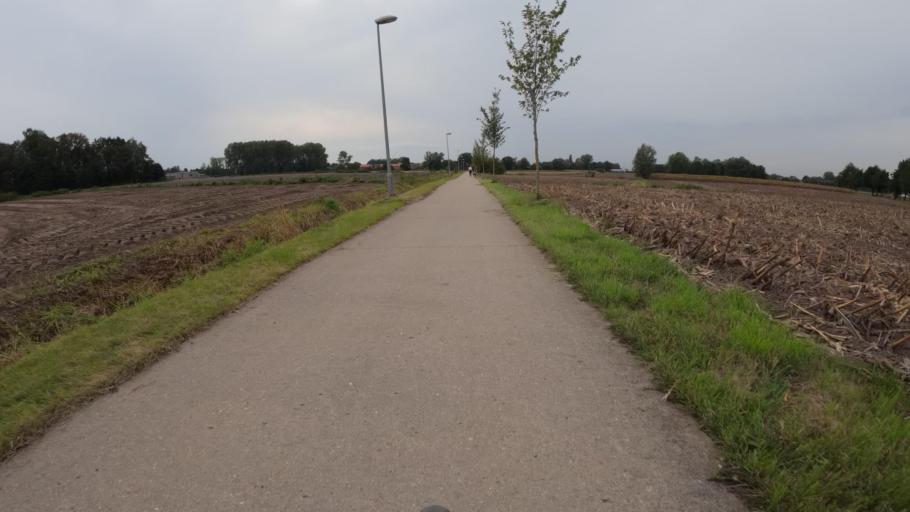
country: BE
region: Flanders
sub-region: Provincie Oost-Vlaanderen
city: Sint-Gillis-Waas
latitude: 51.2155
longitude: 4.0807
